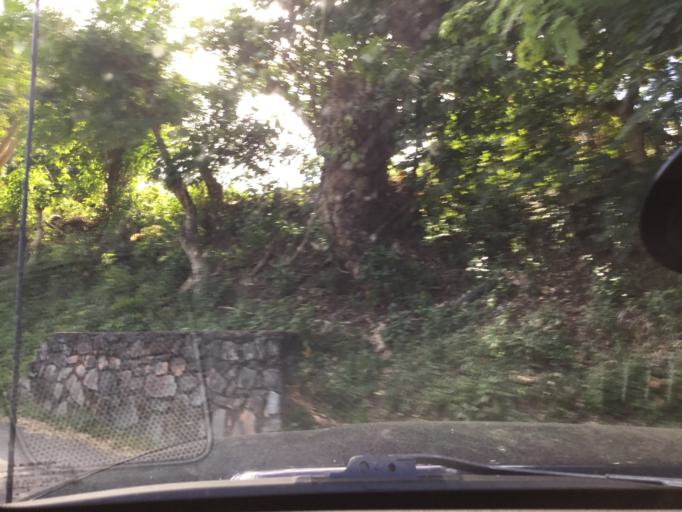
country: VC
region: Saint George
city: Kingstown
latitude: 13.1480
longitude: -61.1751
